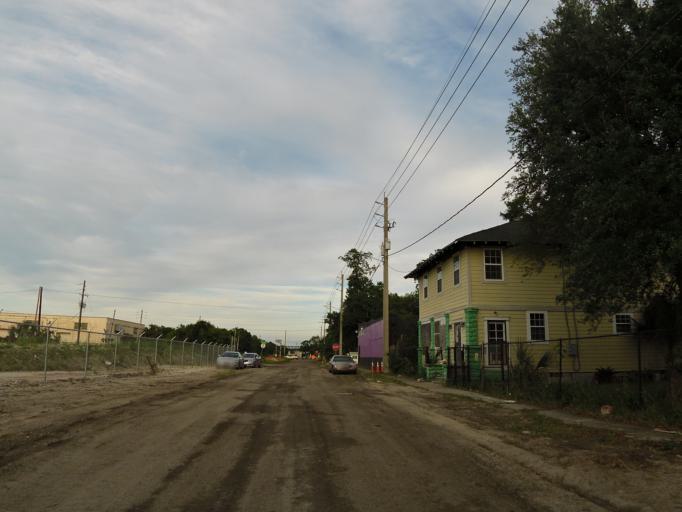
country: US
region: Florida
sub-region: Duval County
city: Jacksonville
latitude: 30.3437
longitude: -81.6439
